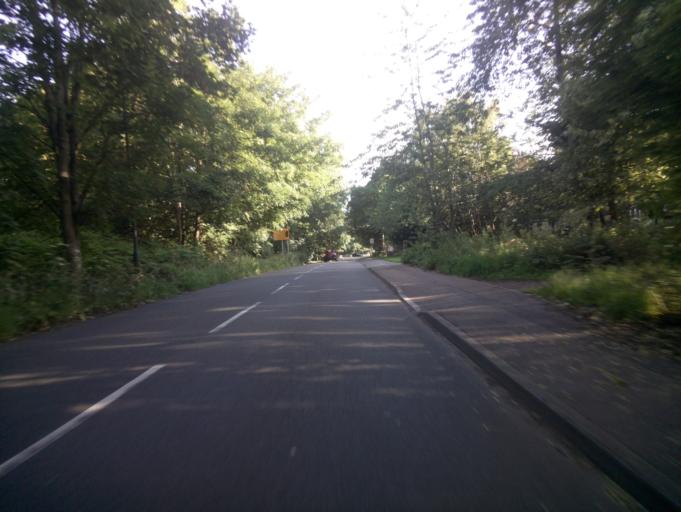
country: GB
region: England
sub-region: South Gloucestershire
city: Mangotsfield
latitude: 51.4779
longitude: -2.4841
